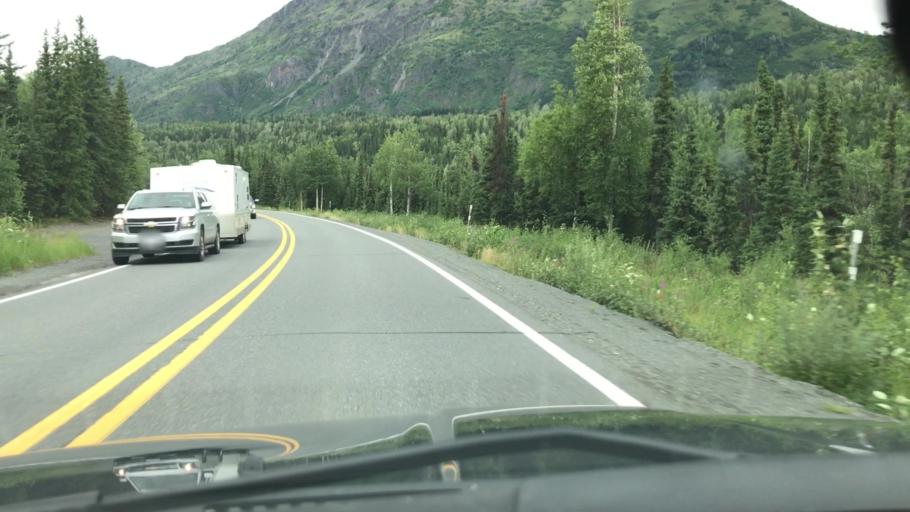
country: US
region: Alaska
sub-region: Kenai Peninsula Borough
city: Seward
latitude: 60.4859
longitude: -149.9635
